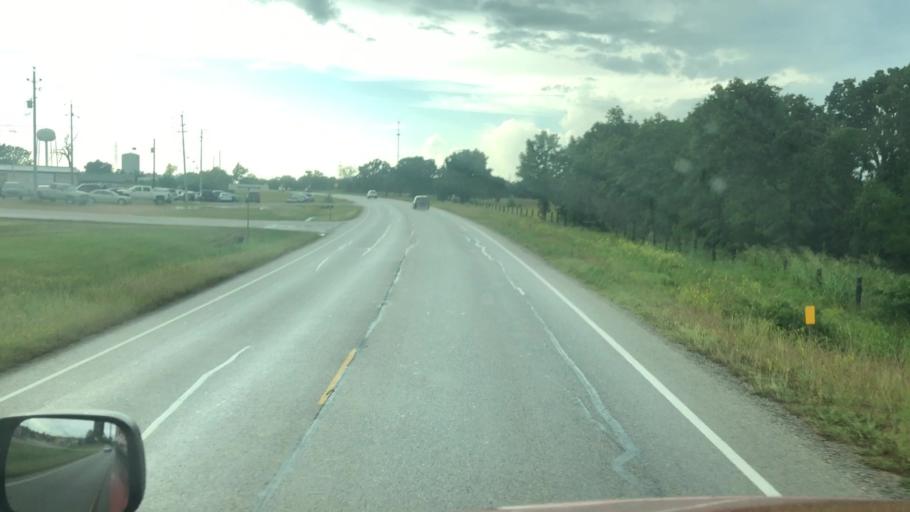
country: US
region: Texas
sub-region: Bastrop County
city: Bastrop
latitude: 30.1071
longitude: -97.2877
